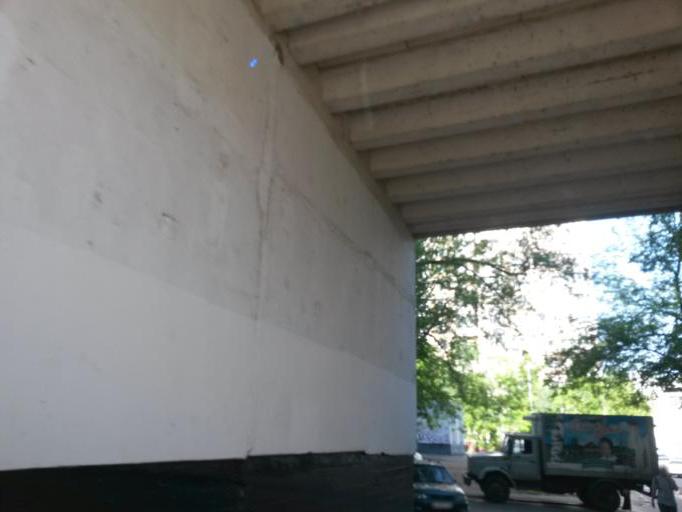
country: RU
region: Moscow
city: Mar'ino
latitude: 55.6454
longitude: 37.7215
